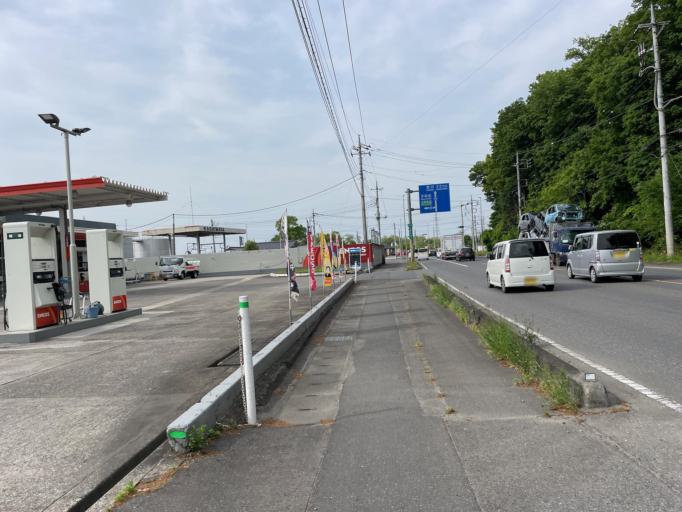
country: JP
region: Tochigi
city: Mibu
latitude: 36.4050
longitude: 139.8038
